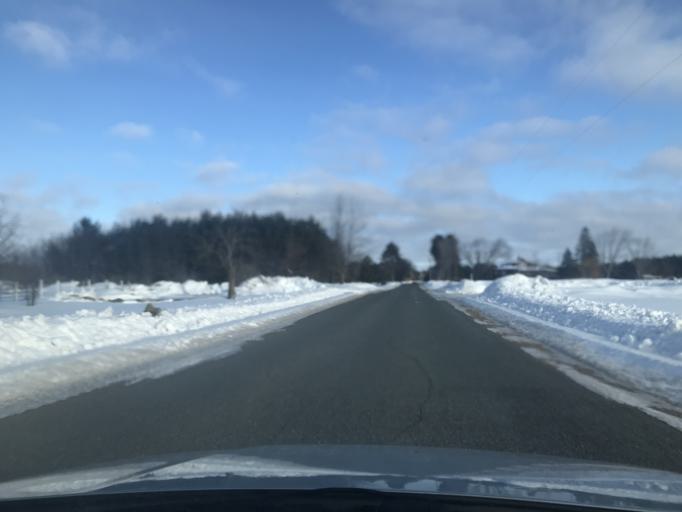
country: US
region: Wisconsin
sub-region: Marinette County
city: Niagara
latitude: 45.6164
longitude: -87.9769
